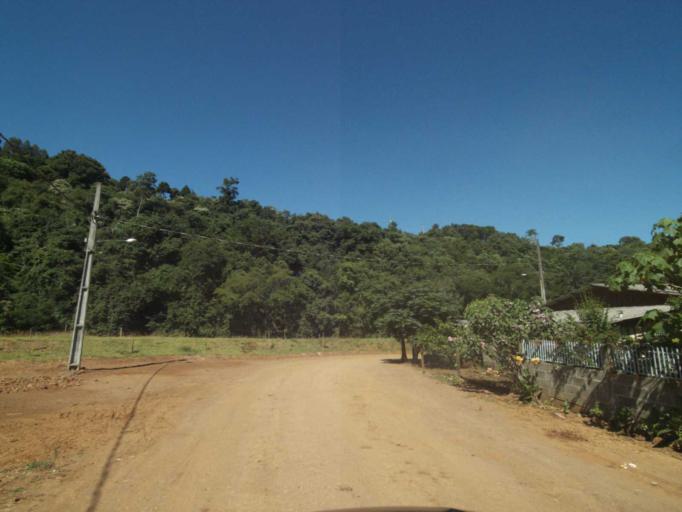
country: BR
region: Parana
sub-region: Francisco Beltrao
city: Francisco Beltrao
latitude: -26.1461
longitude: -53.3068
